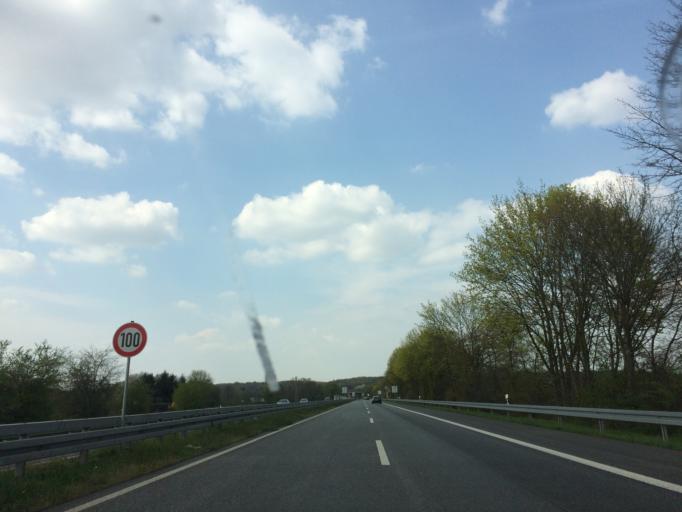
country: DE
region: Hesse
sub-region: Regierungsbezirk Darmstadt
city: Muehlheim am Main
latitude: 50.0912
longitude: 8.8199
